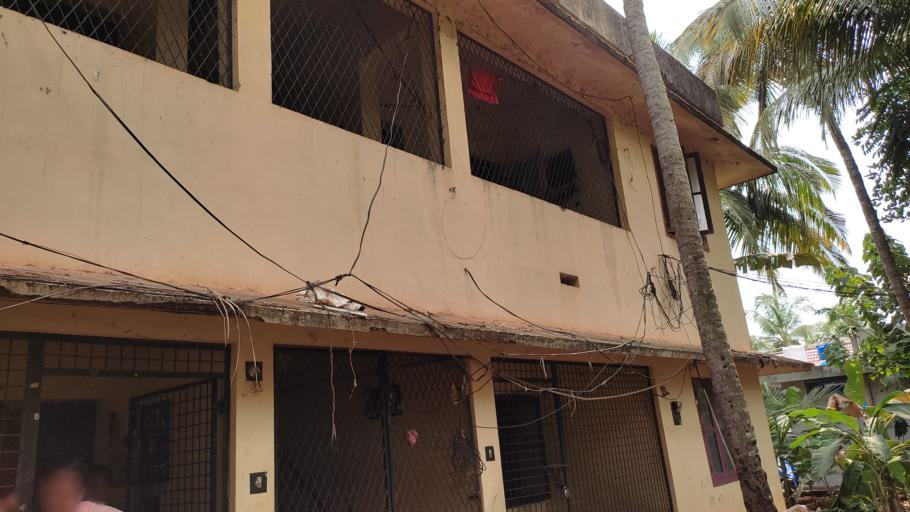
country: IN
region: Kerala
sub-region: Malappuram
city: Ponnani
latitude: 10.8315
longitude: 75.9975
